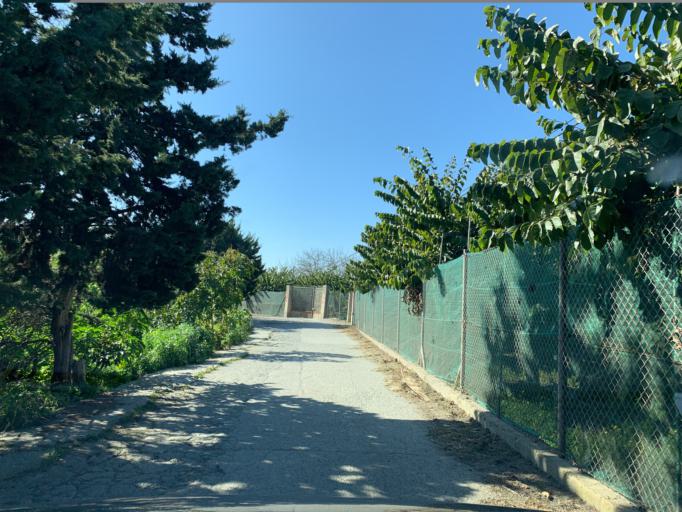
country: ES
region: Andalusia
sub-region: Provincia de Granada
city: El Varadero
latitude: 36.7257
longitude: -3.5567
